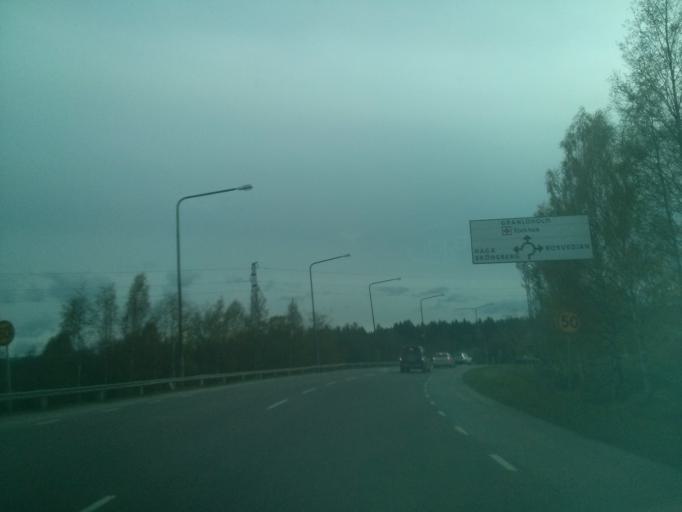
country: SE
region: Vaesternorrland
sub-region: Sundsvalls Kommun
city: Sundsvall
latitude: 62.4115
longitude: 17.3361
